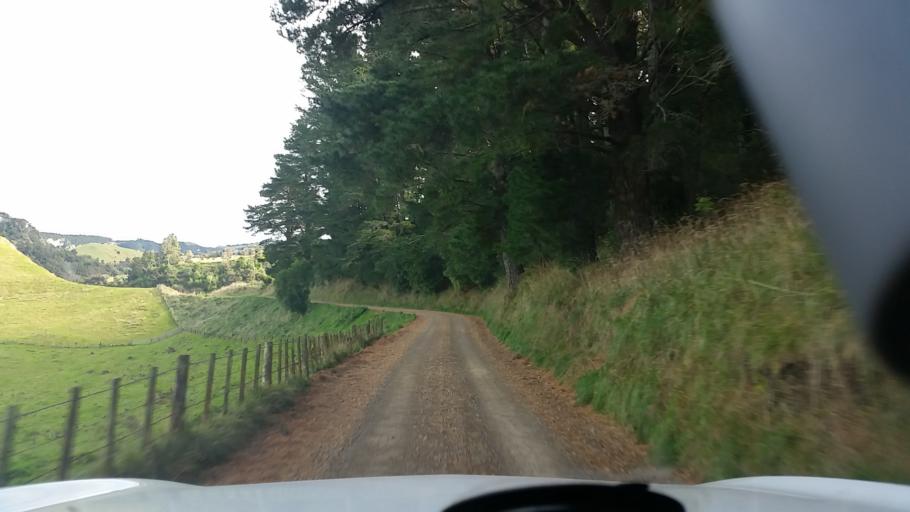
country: NZ
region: Hawke's Bay
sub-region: Napier City
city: Napier
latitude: -39.0954
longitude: 176.8715
